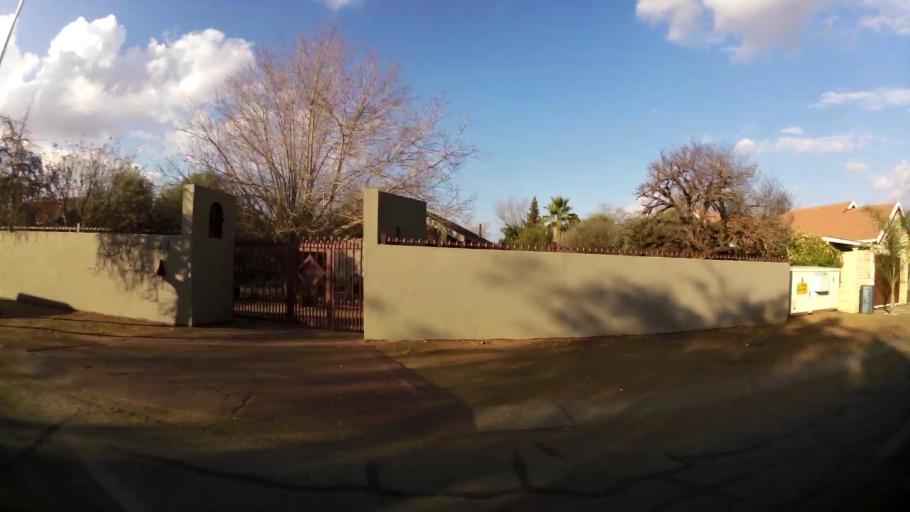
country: ZA
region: Orange Free State
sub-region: Mangaung Metropolitan Municipality
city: Bloemfontein
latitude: -29.1523
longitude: 26.1755
